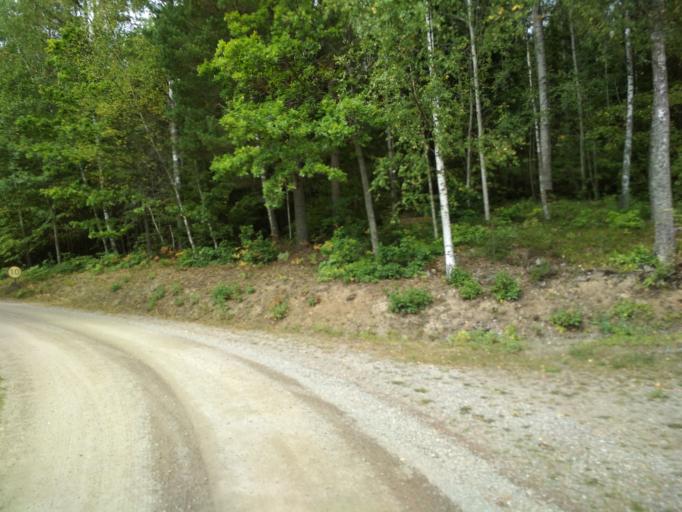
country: SE
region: Soedermanland
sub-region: Eskilstuna Kommun
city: Arla
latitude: 59.1890
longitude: 16.6160
